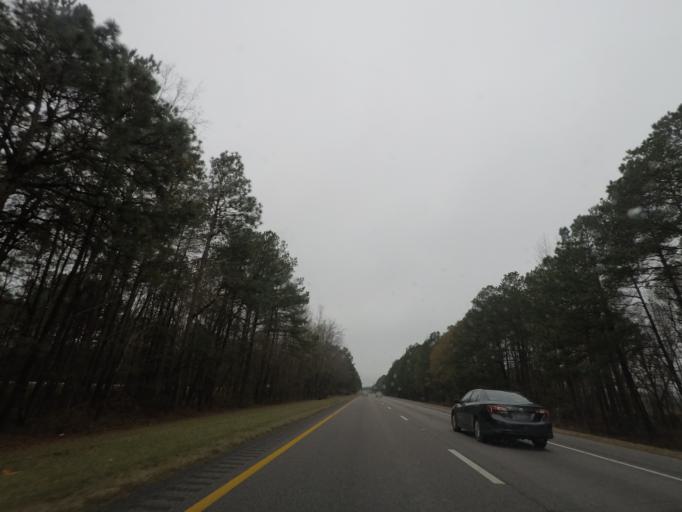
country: US
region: South Carolina
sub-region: Florence County
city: Timmonsville
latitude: 33.9900
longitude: -80.0198
